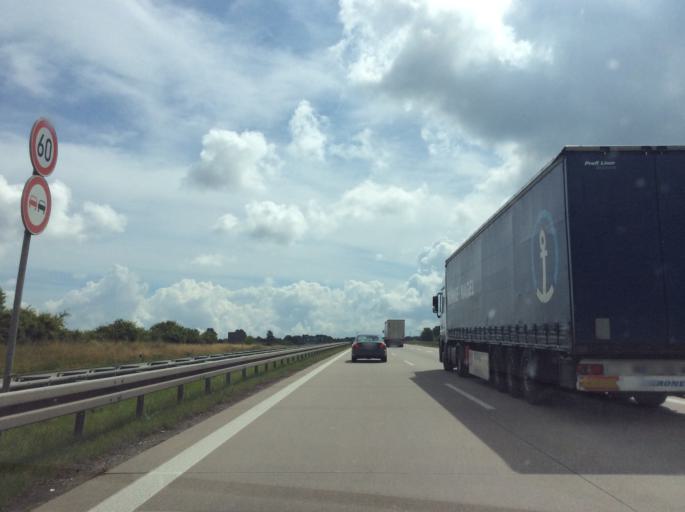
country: DE
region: Brandenburg
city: Mullrose
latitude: 52.3208
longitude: 14.4605
